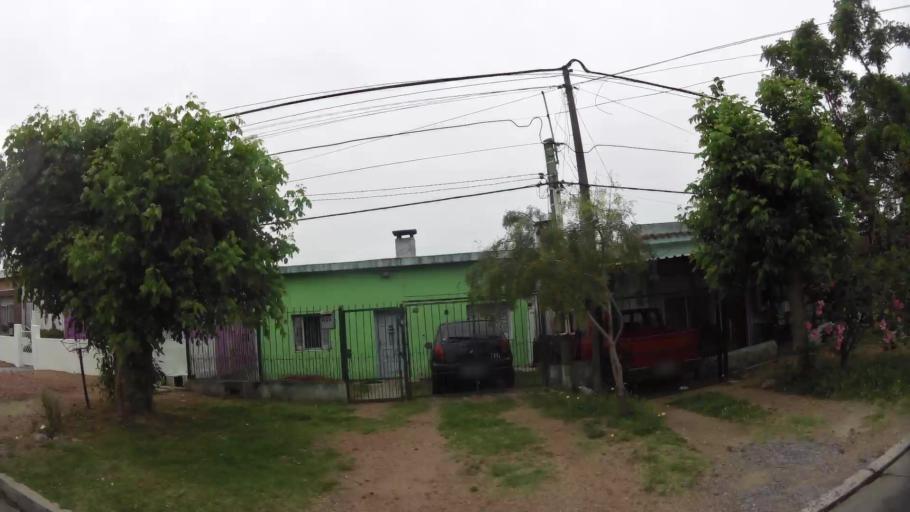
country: UY
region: Canelones
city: Las Piedras
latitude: -34.7292
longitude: -56.2103
